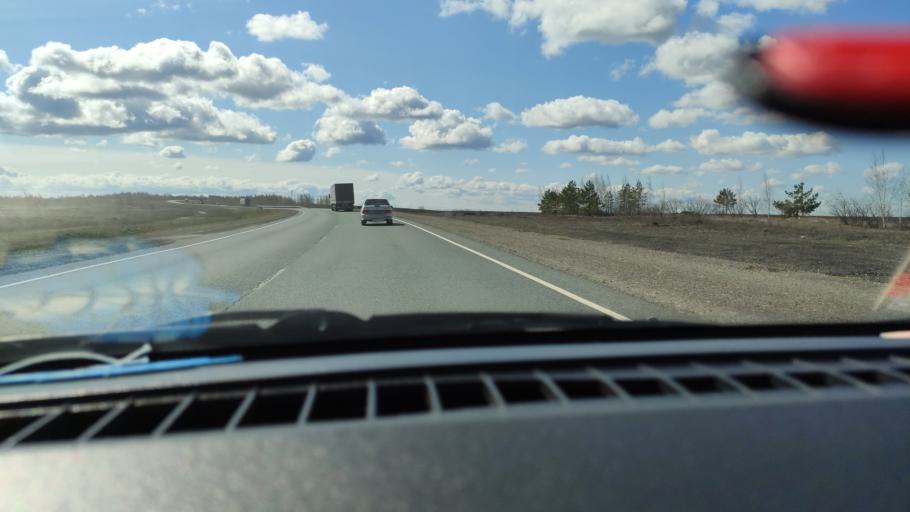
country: RU
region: Samara
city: Syzran'
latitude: 52.9404
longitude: 48.3056
